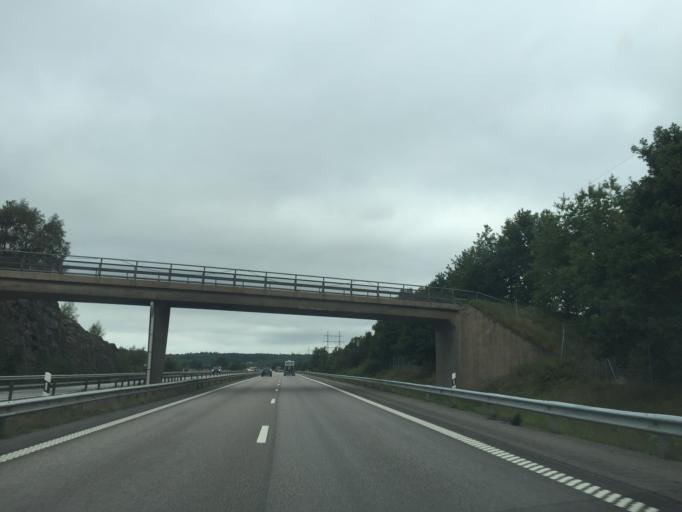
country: SE
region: Halland
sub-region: Kungsbacka Kommun
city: Kungsbacka
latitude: 57.4635
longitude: 12.0760
